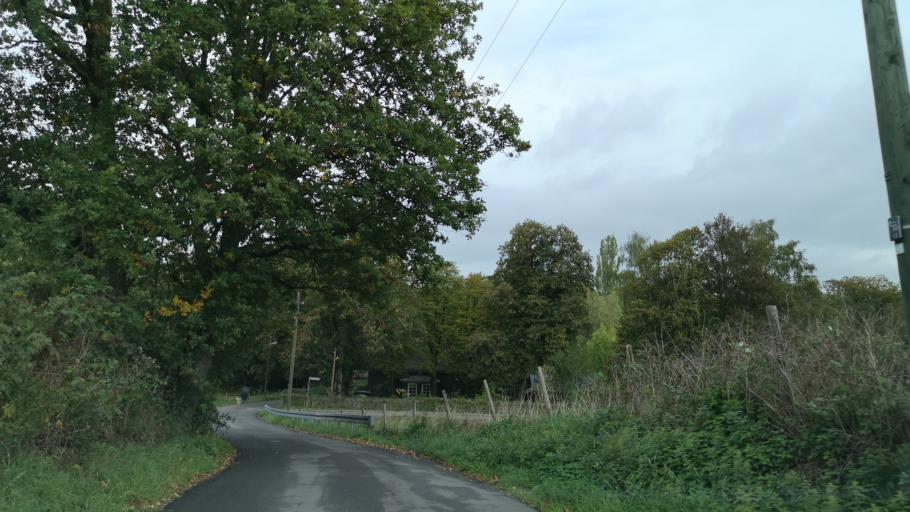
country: DE
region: North Rhine-Westphalia
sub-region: Regierungsbezirk Dusseldorf
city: Velbert
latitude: 51.3763
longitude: 7.0838
